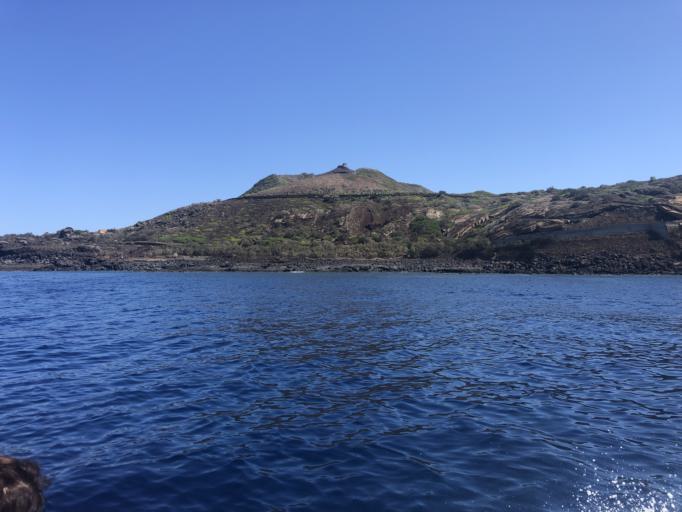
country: IT
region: Sicily
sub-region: Agrigento
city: Lampedusa
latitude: 35.8763
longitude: 12.8668
